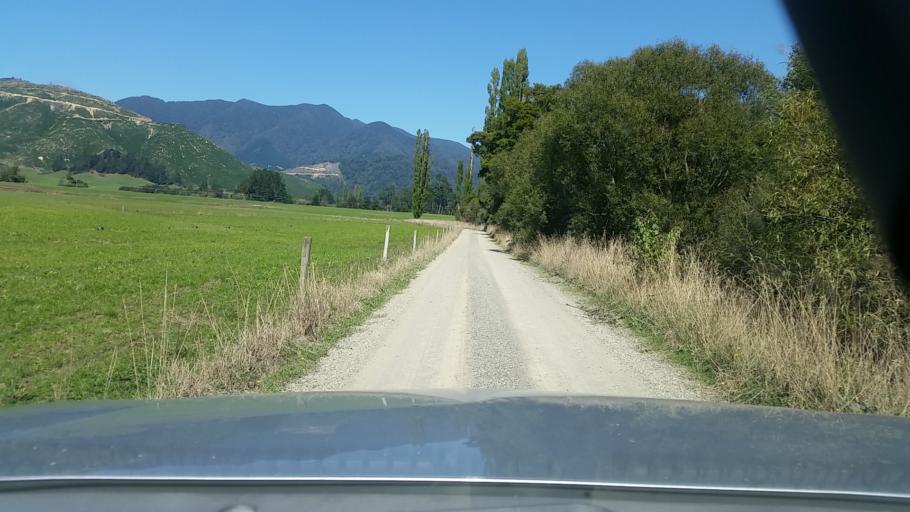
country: NZ
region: Nelson
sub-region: Nelson City
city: Nelson
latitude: -41.2673
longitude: 173.5757
